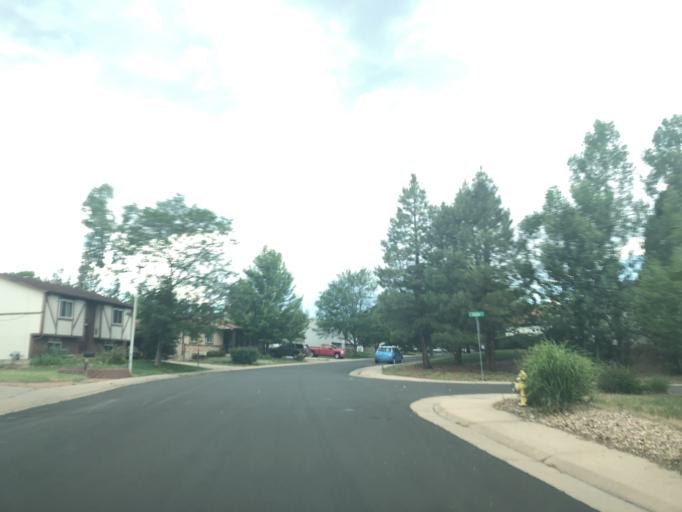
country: US
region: Colorado
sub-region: Arapahoe County
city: Dove Valley
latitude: 39.6263
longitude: -104.7832
